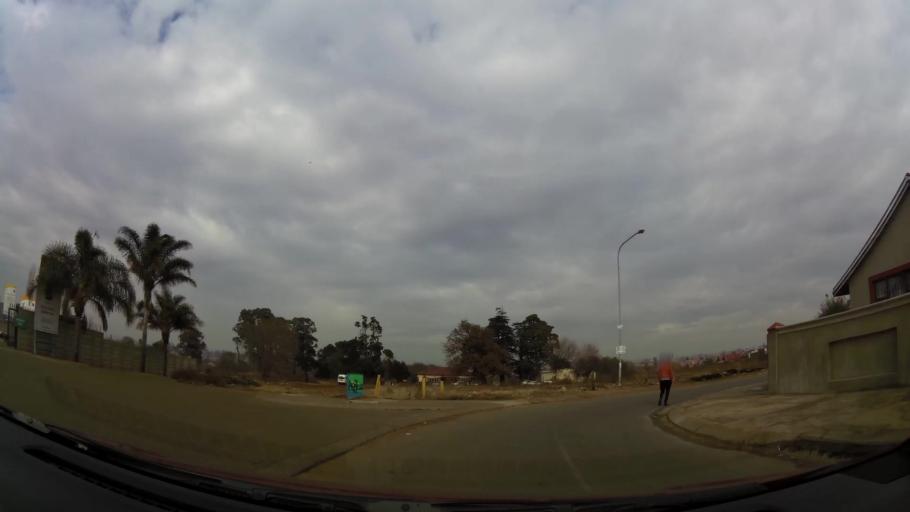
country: ZA
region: Gauteng
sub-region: City of Johannesburg Metropolitan Municipality
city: Soweto
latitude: -26.2782
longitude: 27.8356
